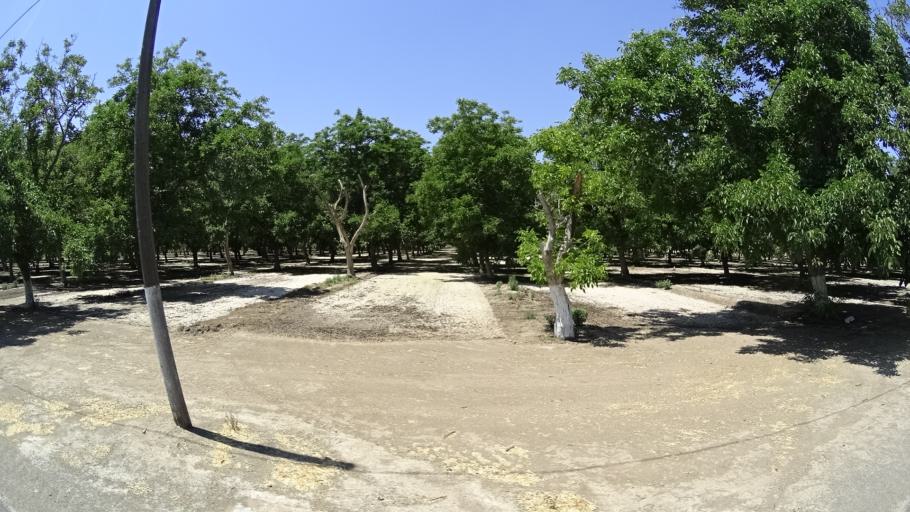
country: US
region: California
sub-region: Kings County
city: Armona
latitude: 36.3366
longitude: -119.7269
